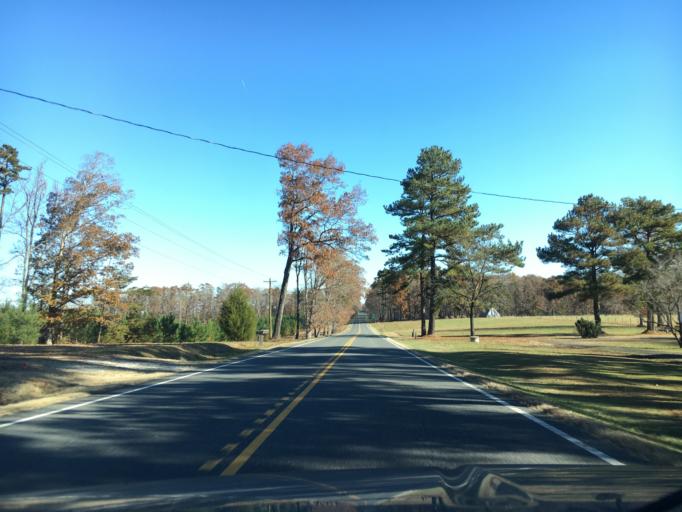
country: US
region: Virginia
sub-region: Buckingham County
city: Buckingham
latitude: 37.4820
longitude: -78.6486
